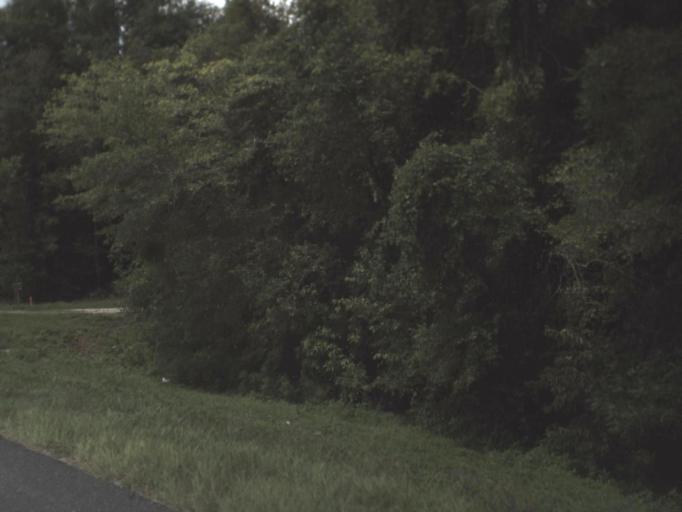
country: US
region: Florida
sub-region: Gilchrist County
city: Trenton
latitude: 29.7819
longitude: -82.8667
